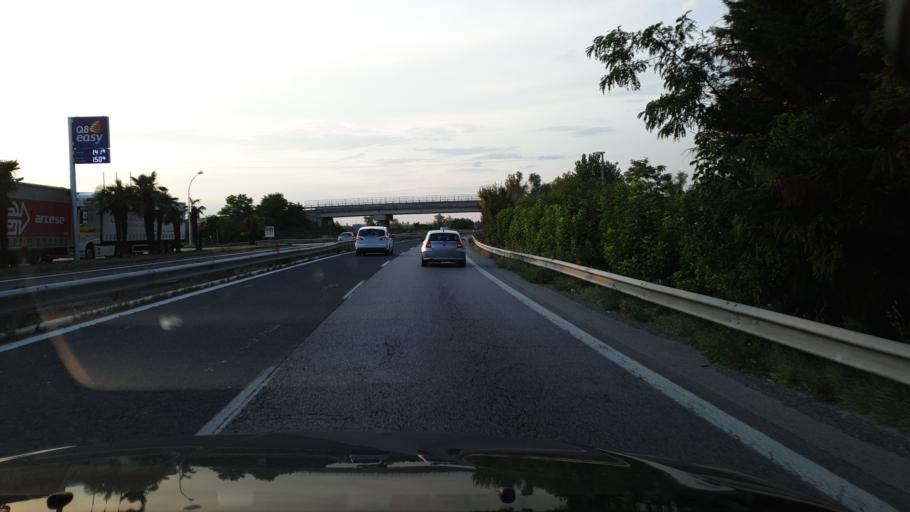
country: IT
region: Emilia-Romagna
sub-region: Forli-Cesena
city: San Mauro a Mare
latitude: 44.1495
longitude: 12.4449
